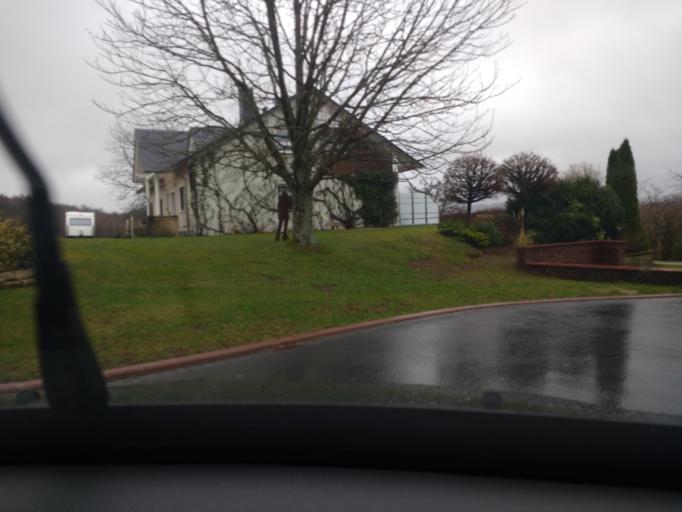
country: DE
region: Rheinland-Pfalz
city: Paschel
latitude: 49.6394
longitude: 6.6896
